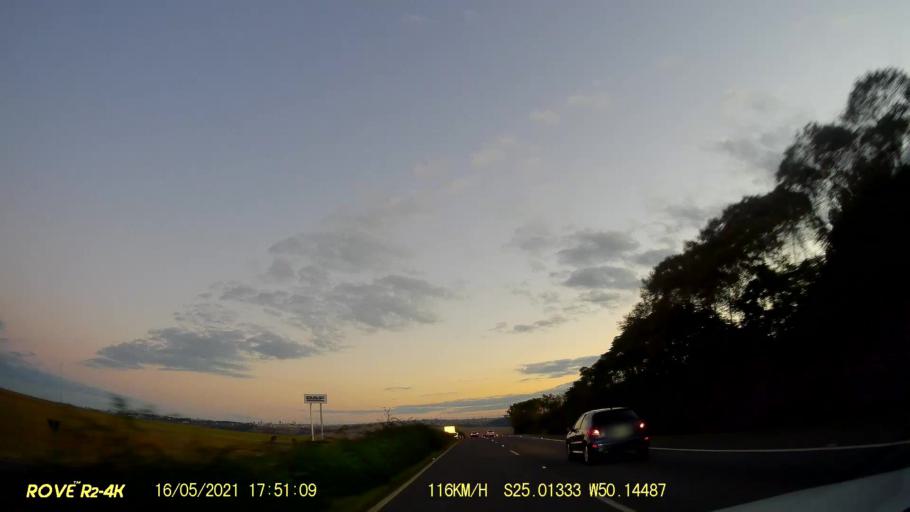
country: BR
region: Parana
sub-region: Carambei
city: Carambei
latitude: -25.0134
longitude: -50.1448
